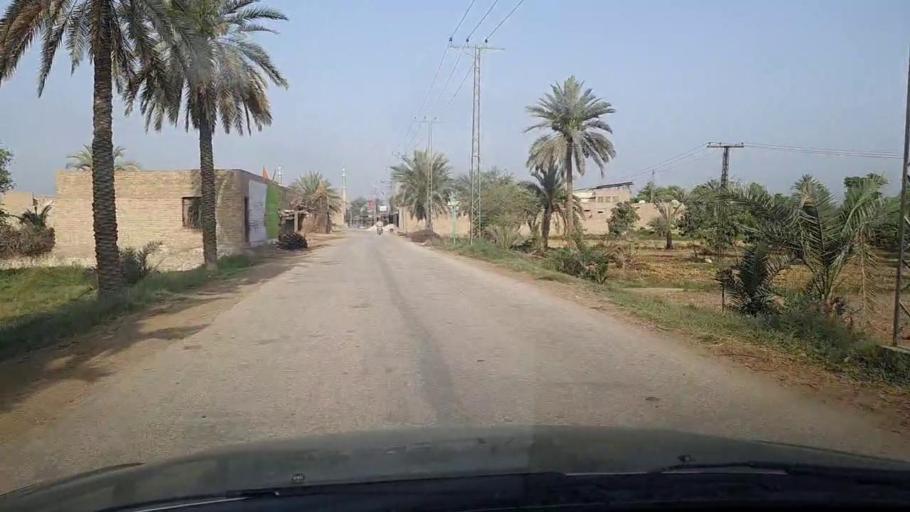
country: PK
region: Sindh
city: Pir jo Goth
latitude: 27.5712
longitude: 68.6143
